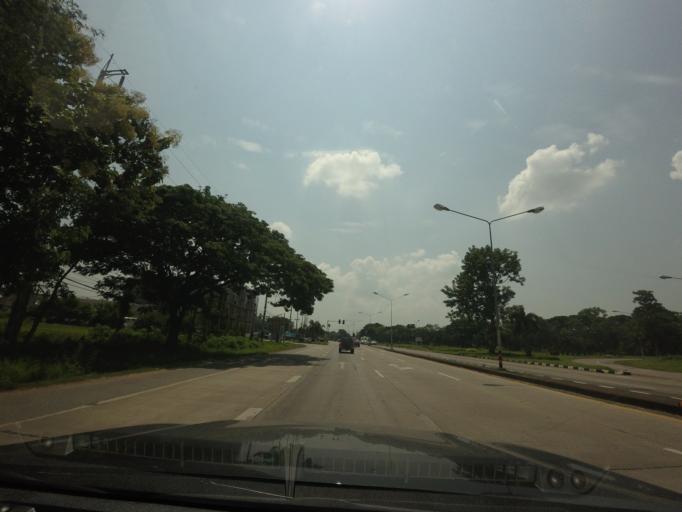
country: TH
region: Uttaradit
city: Uttaradit
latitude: 17.6092
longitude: 100.1232
